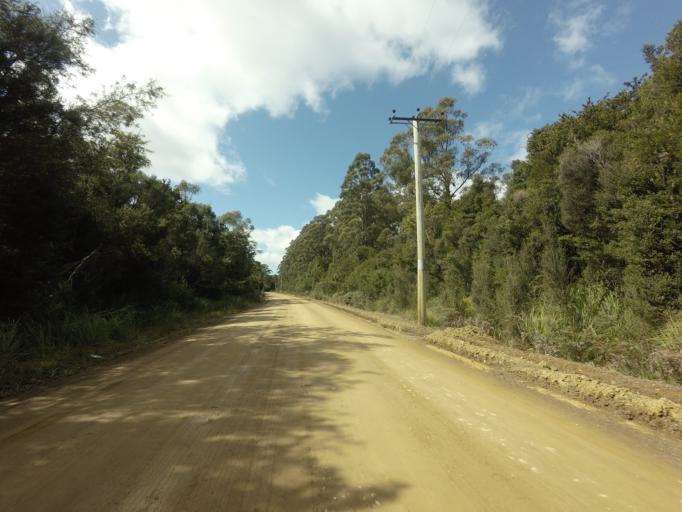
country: AU
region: Tasmania
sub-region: Huon Valley
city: Geeveston
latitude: -43.4140
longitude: 146.8938
